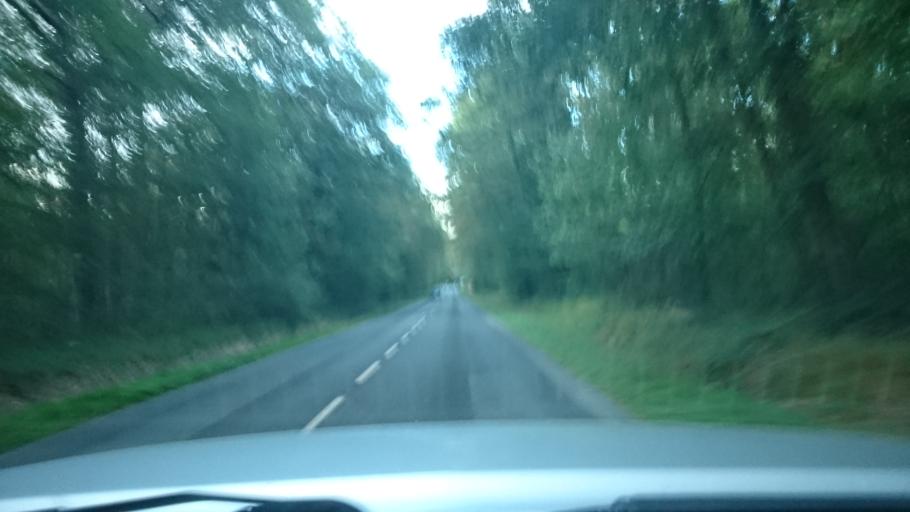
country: FR
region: Ile-de-France
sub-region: Departement de Seine-et-Marne
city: Samois-sur-Seine
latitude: 48.4652
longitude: 2.7354
